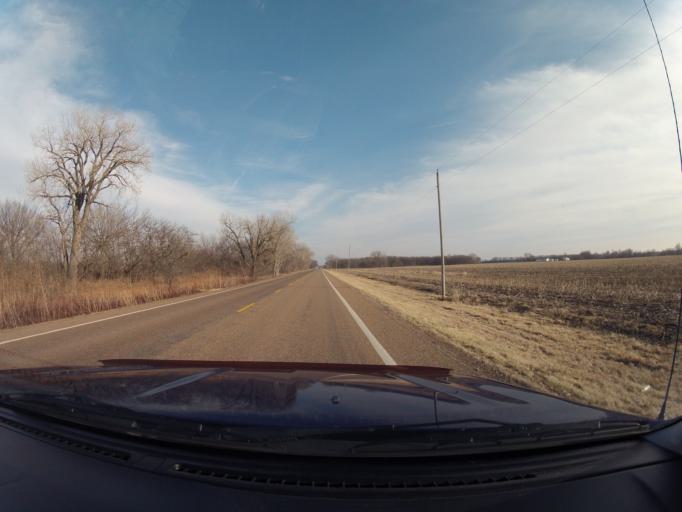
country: US
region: Kansas
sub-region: Pottawatomie County
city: Saint Marys
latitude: 39.2088
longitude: -96.1053
